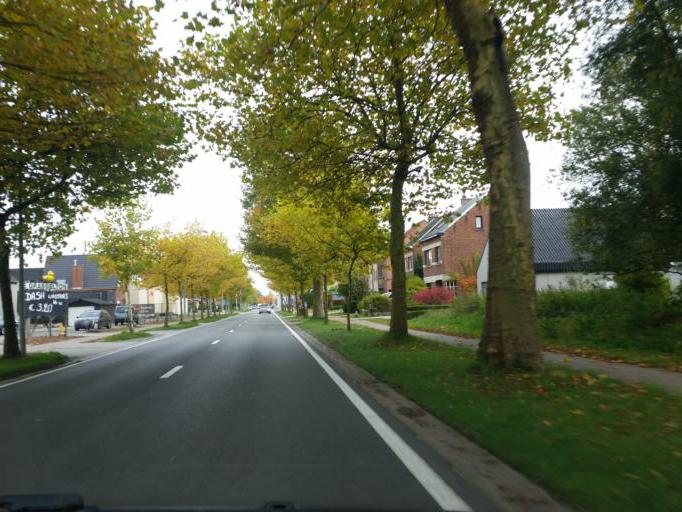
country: BE
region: Flanders
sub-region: Provincie Antwerpen
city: Bonheiden
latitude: 51.0384
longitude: 4.5821
